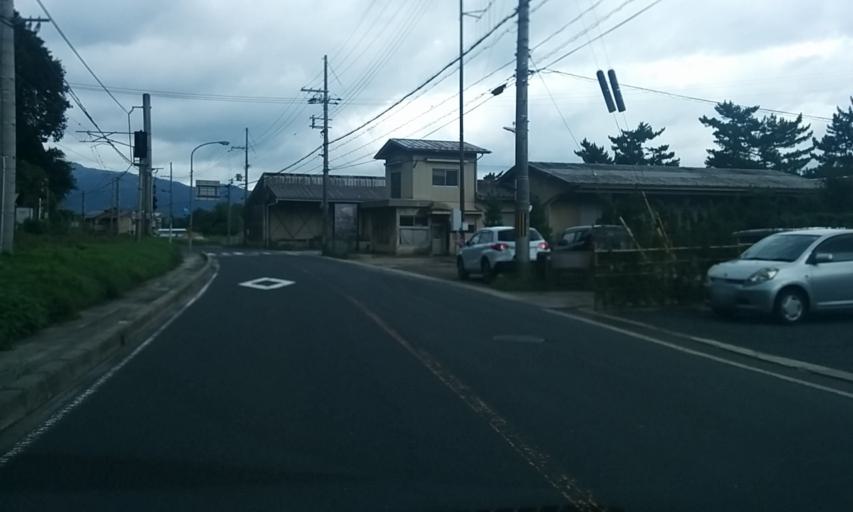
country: JP
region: Kyoto
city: Miyazu
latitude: 35.5491
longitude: 135.1872
